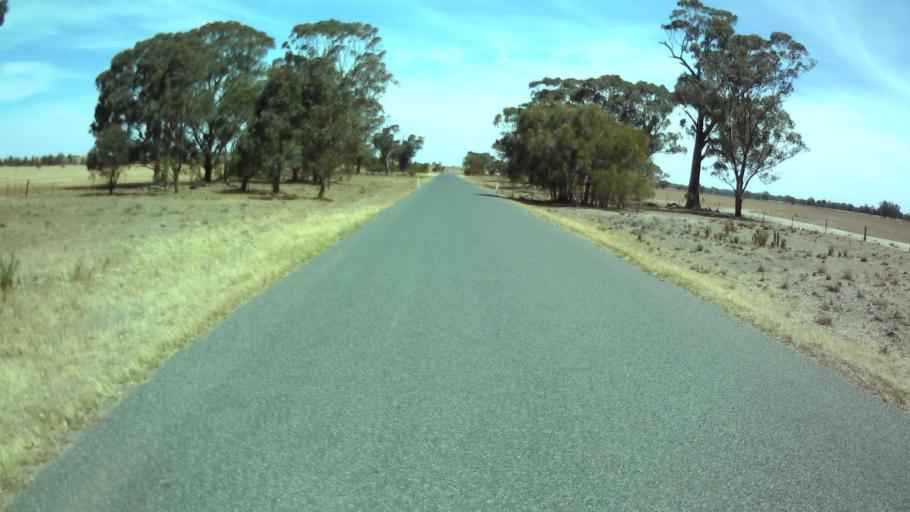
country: AU
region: New South Wales
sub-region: Weddin
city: Grenfell
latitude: -33.8831
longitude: 147.7425
